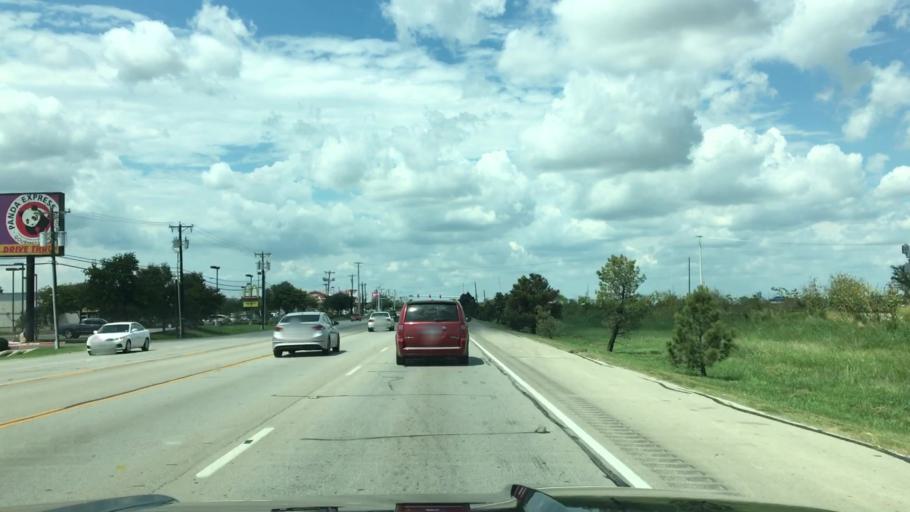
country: US
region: Texas
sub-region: Tarrant County
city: Saginaw
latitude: 32.8785
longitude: -97.3796
